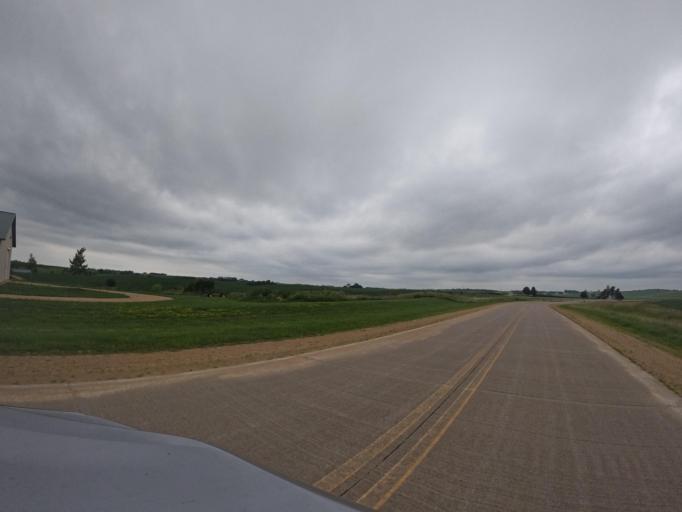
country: US
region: Iowa
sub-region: Jackson County
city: Maquoketa
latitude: 41.9493
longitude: -90.6299
